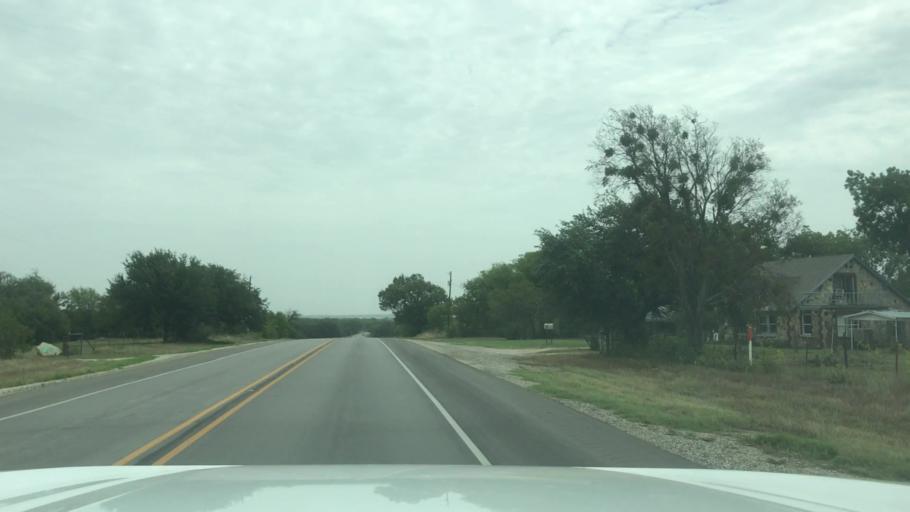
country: US
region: Texas
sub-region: Erath County
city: Dublin
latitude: 32.0864
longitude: -98.3128
